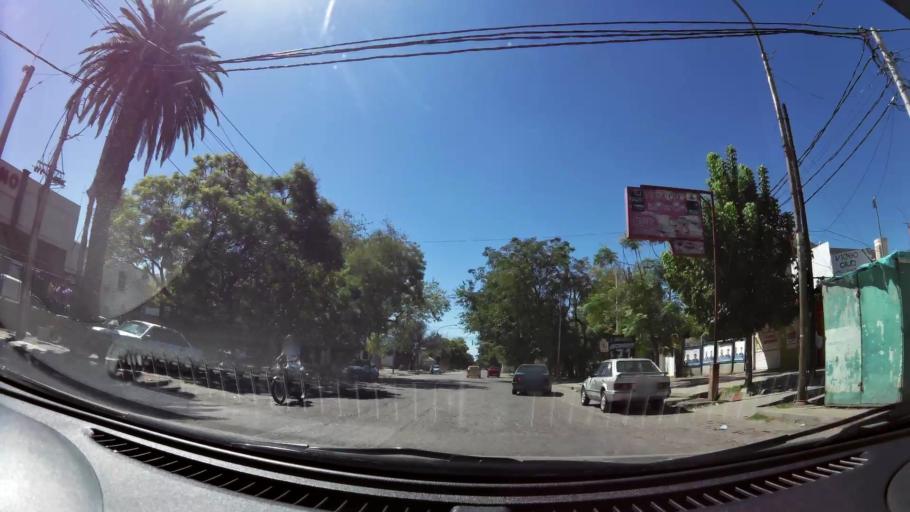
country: AR
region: Mendoza
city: Las Heras
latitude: -32.8417
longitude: -68.8337
